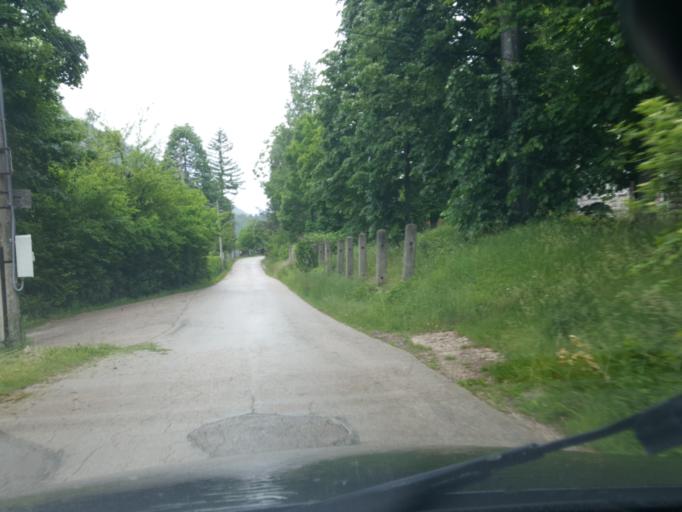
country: RS
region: Central Serbia
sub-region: Zajecarski Okrug
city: Boljevac
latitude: 43.7700
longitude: 21.9353
